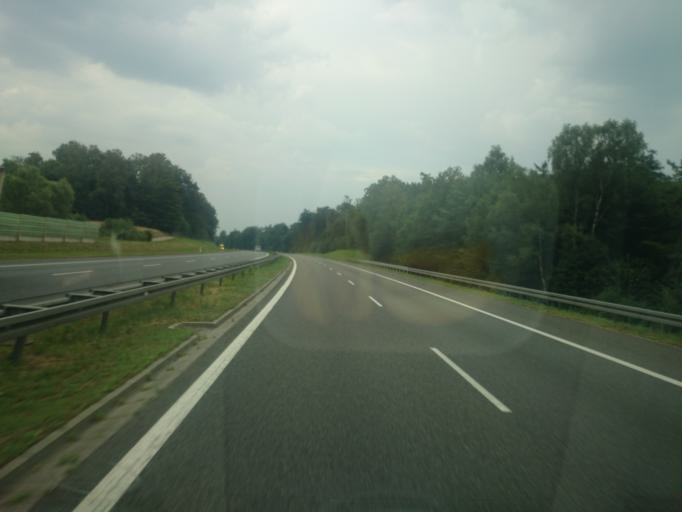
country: PL
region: Opole Voivodeship
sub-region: Powiat strzelecki
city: Ujazd
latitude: 50.4336
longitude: 18.3684
